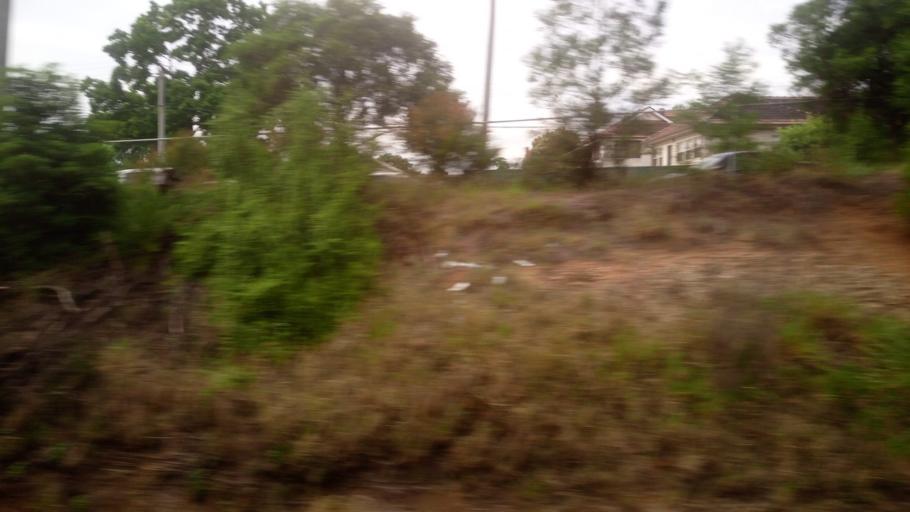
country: AU
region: New South Wales
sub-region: Parramatta
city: Constitution Hill
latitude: -33.8080
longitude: 150.9805
